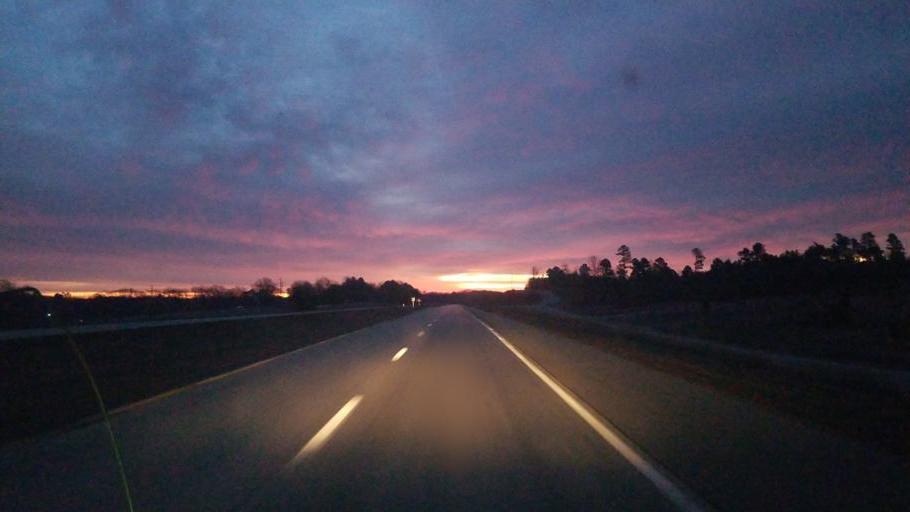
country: US
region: Missouri
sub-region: Shannon County
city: Winona
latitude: 36.9987
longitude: -91.4669
